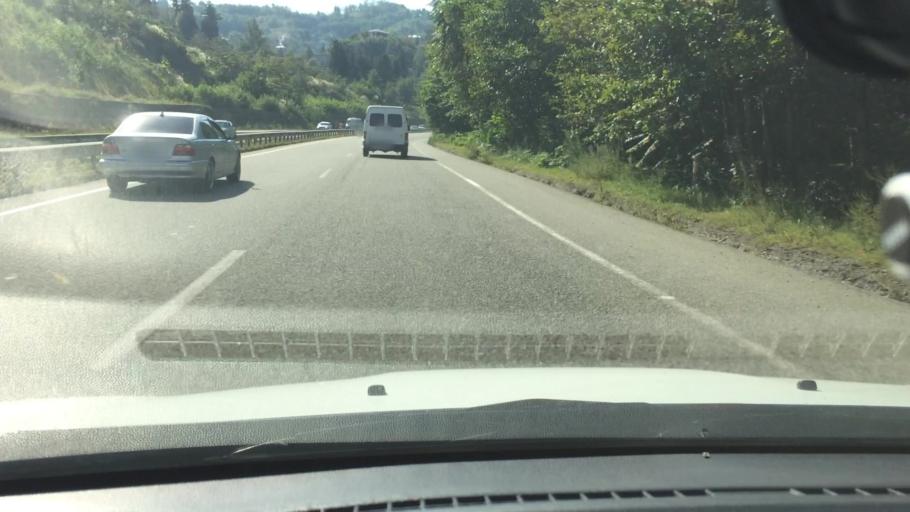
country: GE
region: Ajaria
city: Makhinjauri
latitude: 41.6971
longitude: 41.7274
